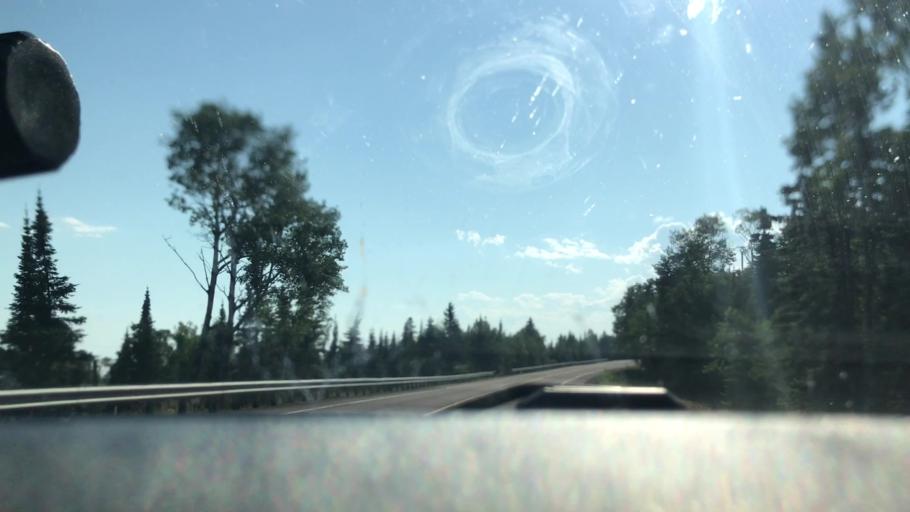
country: US
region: Minnesota
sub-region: Cook County
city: Grand Marais
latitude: 47.8293
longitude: -89.9895
